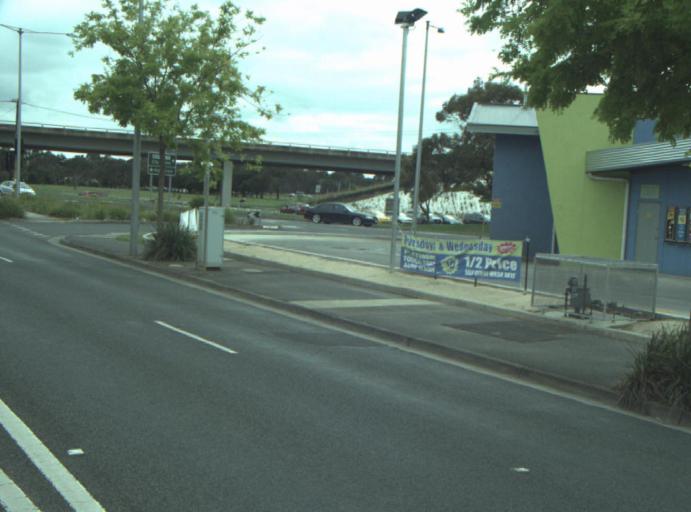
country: AU
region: Victoria
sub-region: Greater Geelong
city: Breakwater
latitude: -38.1682
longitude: 144.3500
